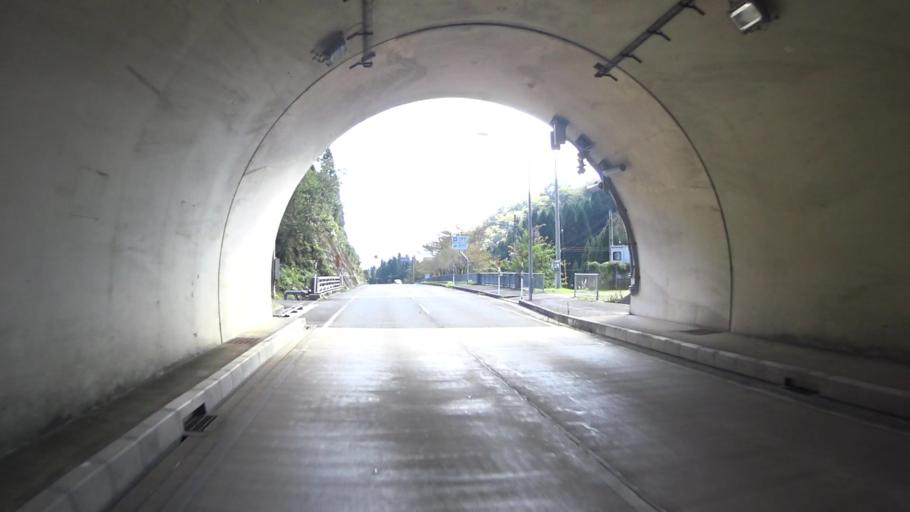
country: JP
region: Hyogo
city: Toyooka
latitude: 35.5242
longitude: 134.9870
